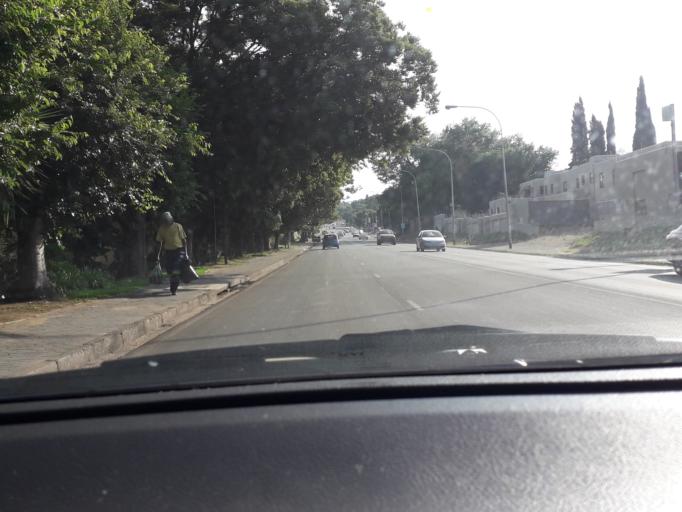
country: ZA
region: Gauteng
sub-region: City of Johannesburg Metropolitan Municipality
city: Modderfontein
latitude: -26.1297
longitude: 28.1018
